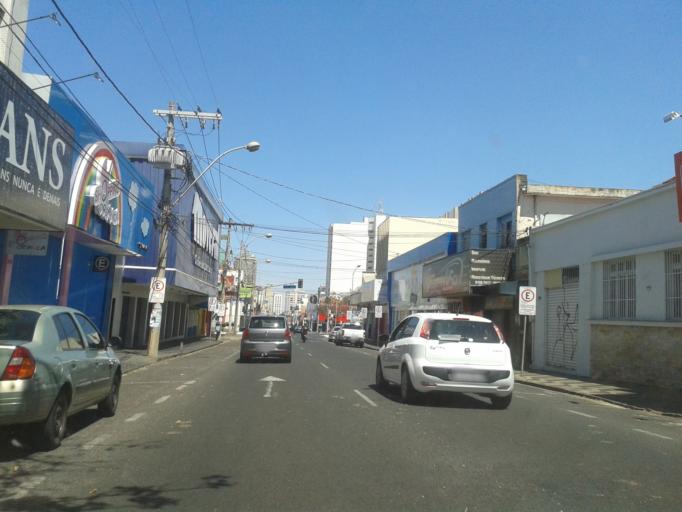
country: BR
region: Minas Gerais
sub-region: Uberlandia
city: Uberlandia
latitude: -18.9155
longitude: -48.2738
